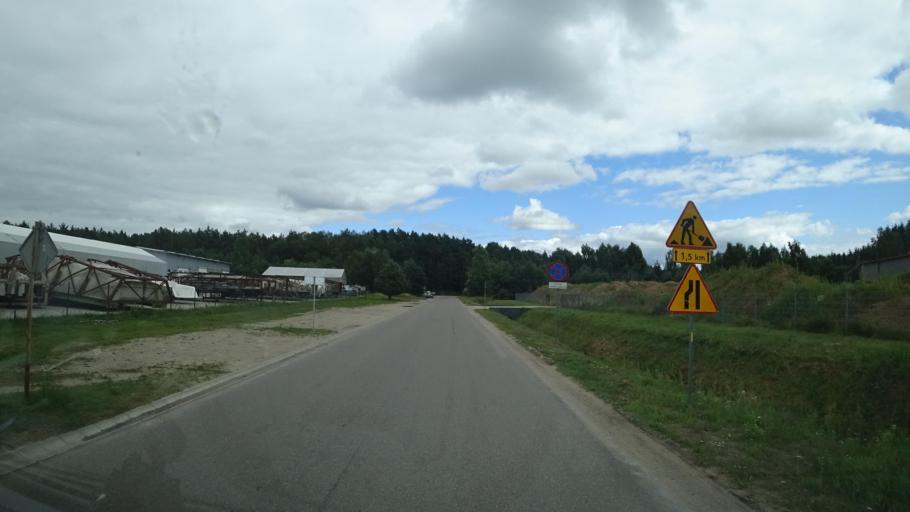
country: PL
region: Warmian-Masurian Voivodeship
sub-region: Powiat goldapski
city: Goldap
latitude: 54.3336
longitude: 22.2922
